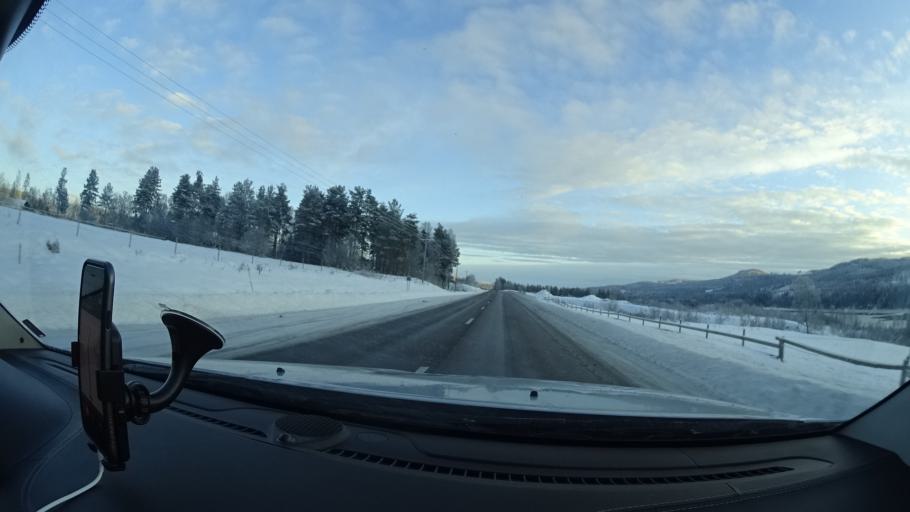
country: SE
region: Jaemtland
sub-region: Ragunda Kommun
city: Hammarstrand
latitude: 63.1456
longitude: 16.1339
